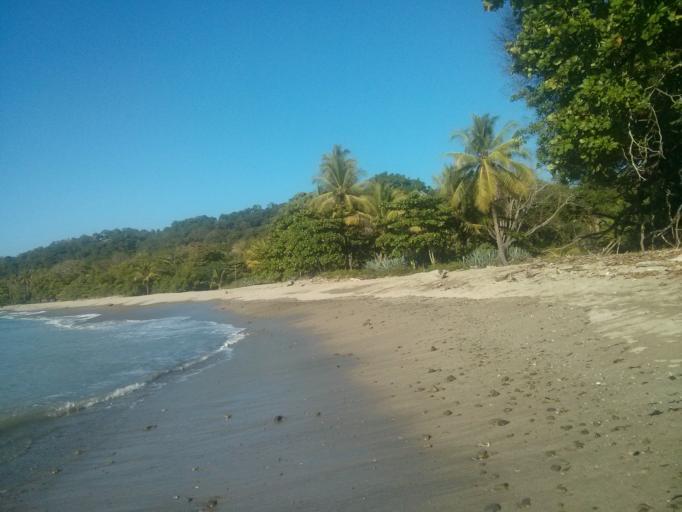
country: CR
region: Puntarenas
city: Paquera
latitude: 9.6110
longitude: -85.1444
